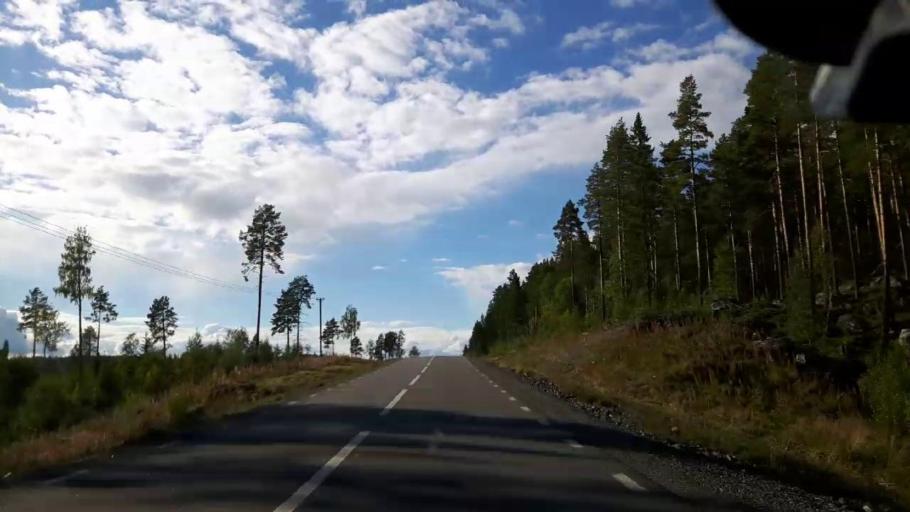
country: SE
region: Jaemtland
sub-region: Stroemsunds Kommun
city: Stroemsund
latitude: 63.5561
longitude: 15.8238
